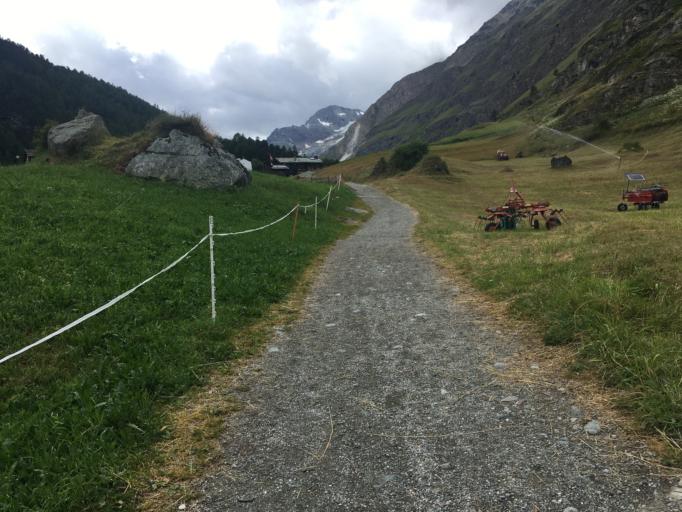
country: CH
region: Valais
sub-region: Visp District
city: Zermatt
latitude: 46.0068
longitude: 7.7185
